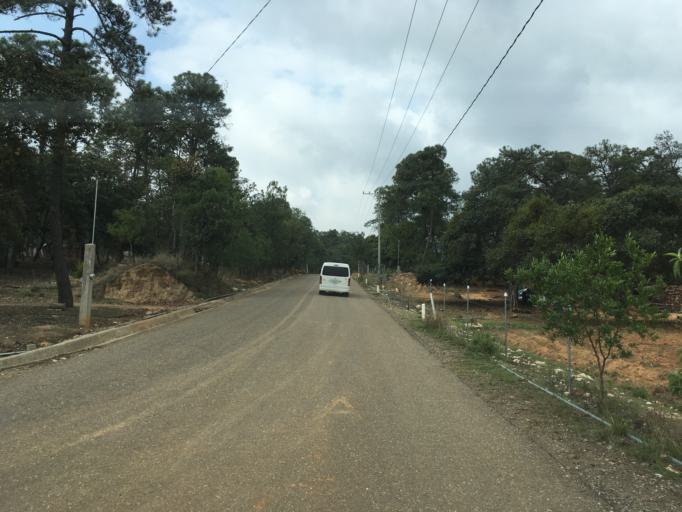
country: MX
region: Oaxaca
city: Santiago Tilantongo
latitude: 17.2169
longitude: -97.2788
